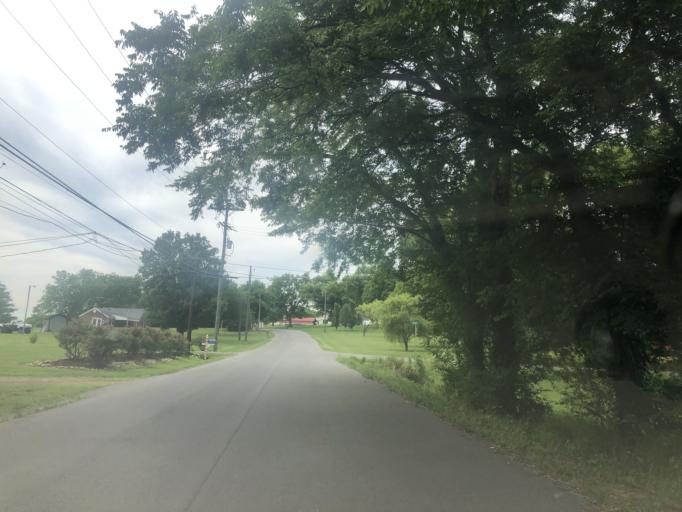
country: US
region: Tennessee
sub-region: Davidson County
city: Lakewood
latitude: 36.2301
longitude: -86.6596
